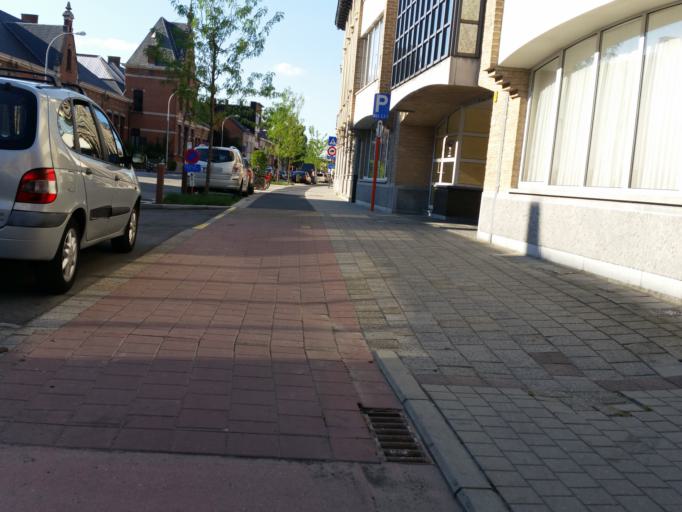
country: BE
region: Flanders
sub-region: Provincie Antwerpen
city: Mechelen
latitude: 51.0152
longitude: 4.4729
